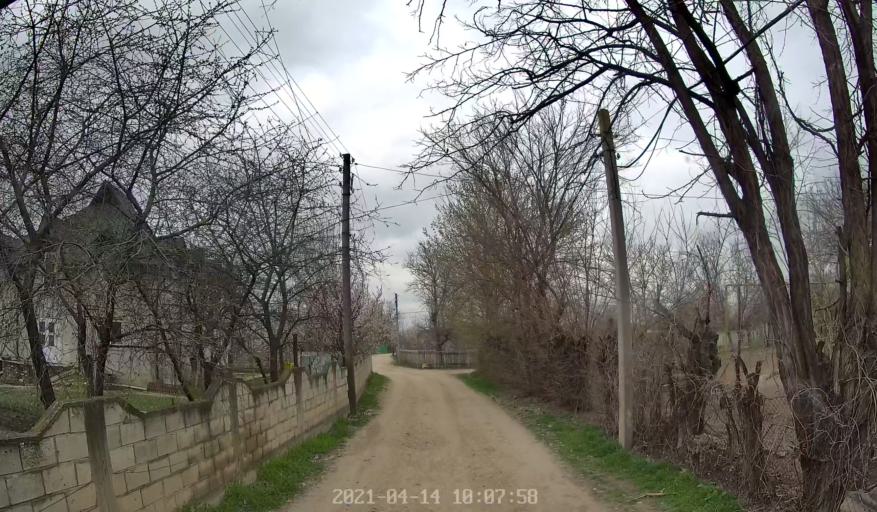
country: MD
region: Criuleni
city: Criuleni
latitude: 47.1447
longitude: 29.1290
